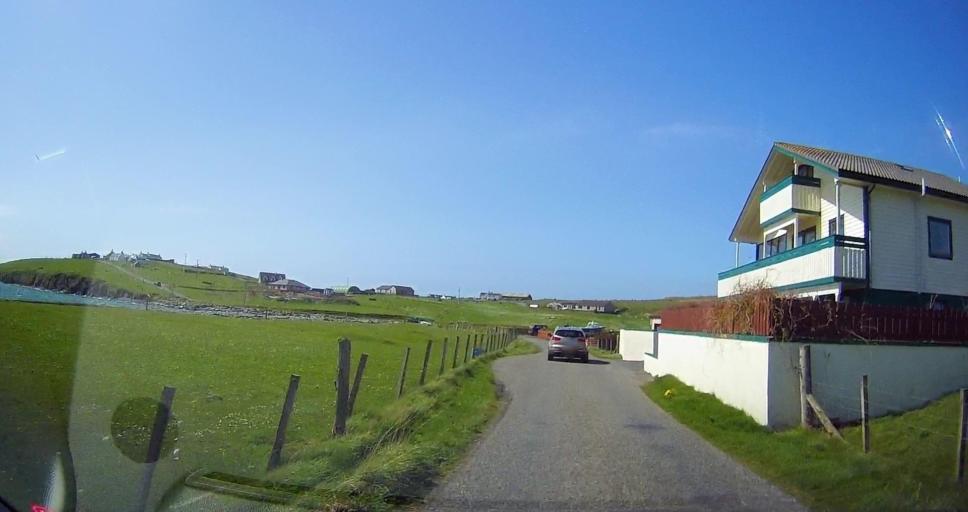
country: GB
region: Scotland
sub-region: Shetland Islands
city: Sandwick
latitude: 60.0651
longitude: -1.3380
